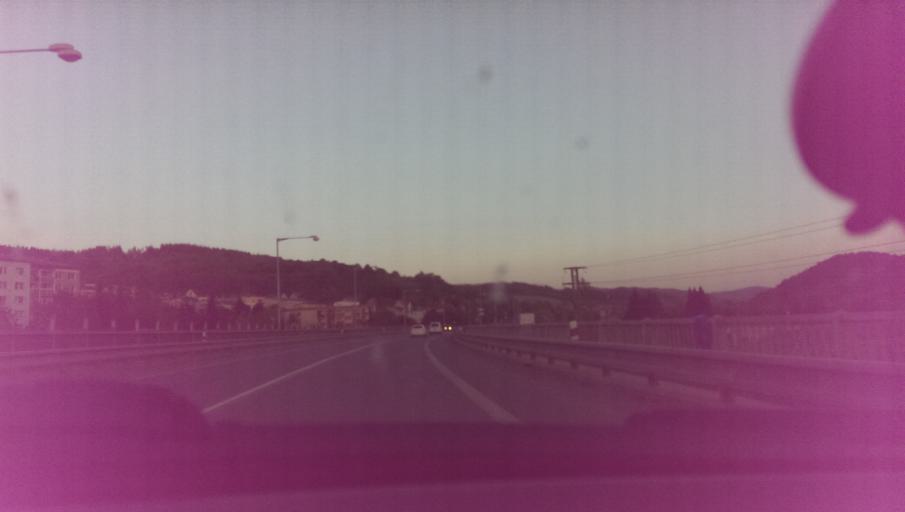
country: CZ
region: Zlin
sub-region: Okres Vsetin
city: Vsetin
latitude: 49.3277
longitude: 18.0006
